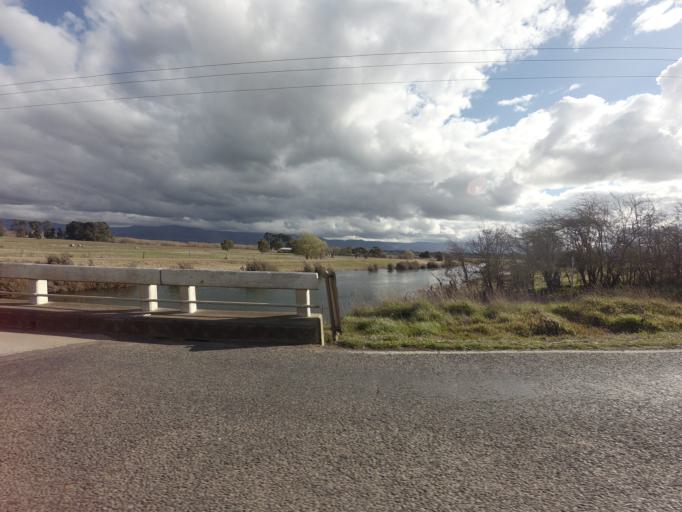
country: AU
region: Tasmania
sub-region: Northern Midlands
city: Longford
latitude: -41.7124
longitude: 147.0824
